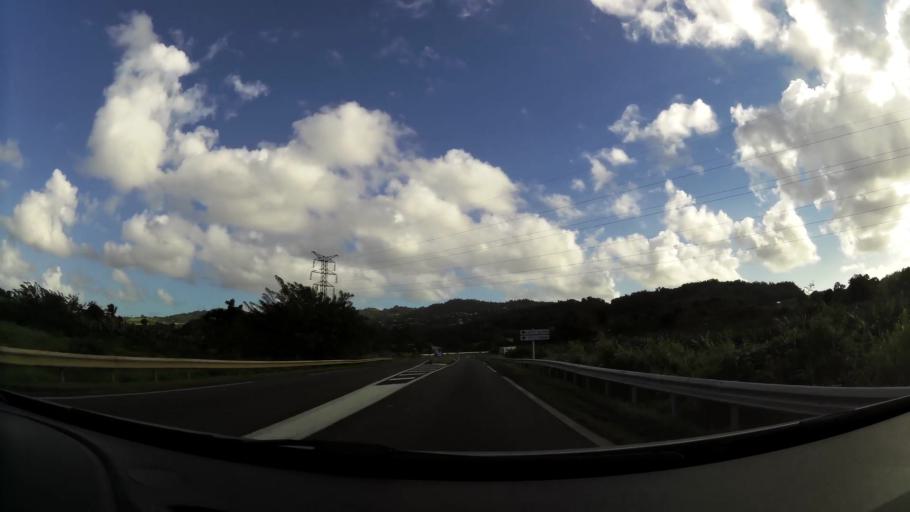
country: MQ
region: Martinique
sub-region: Martinique
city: Ducos
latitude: 14.6009
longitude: -60.9657
